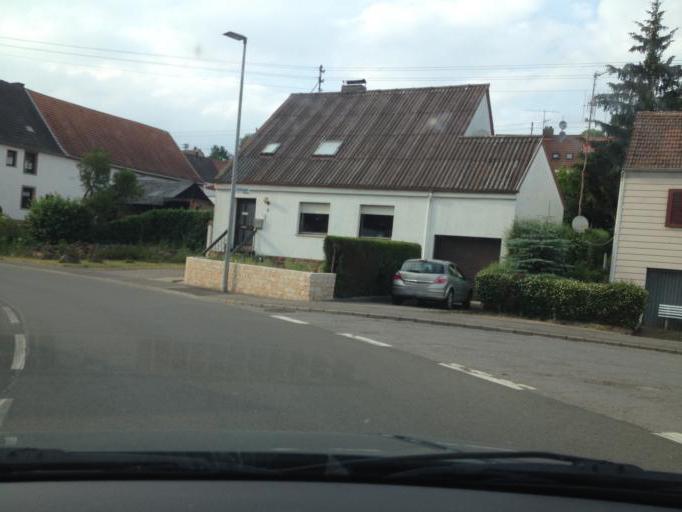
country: DE
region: Saarland
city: Ottweiler
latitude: 49.4324
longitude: 7.1618
